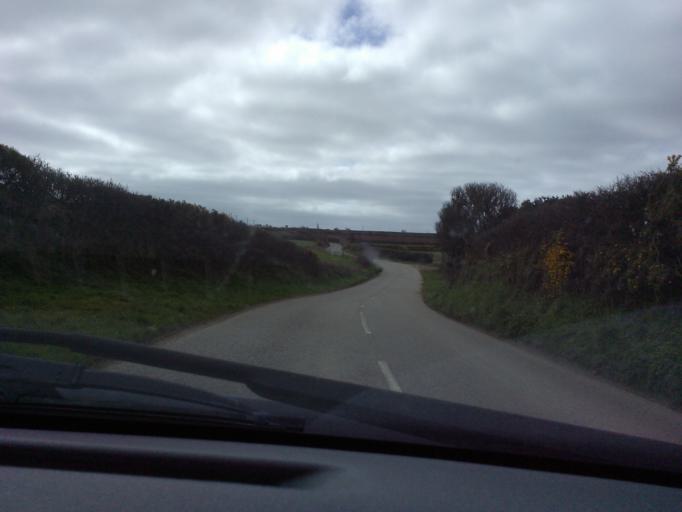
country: GB
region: England
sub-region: Cornwall
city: Penzance
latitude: 50.0828
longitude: -5.5579
